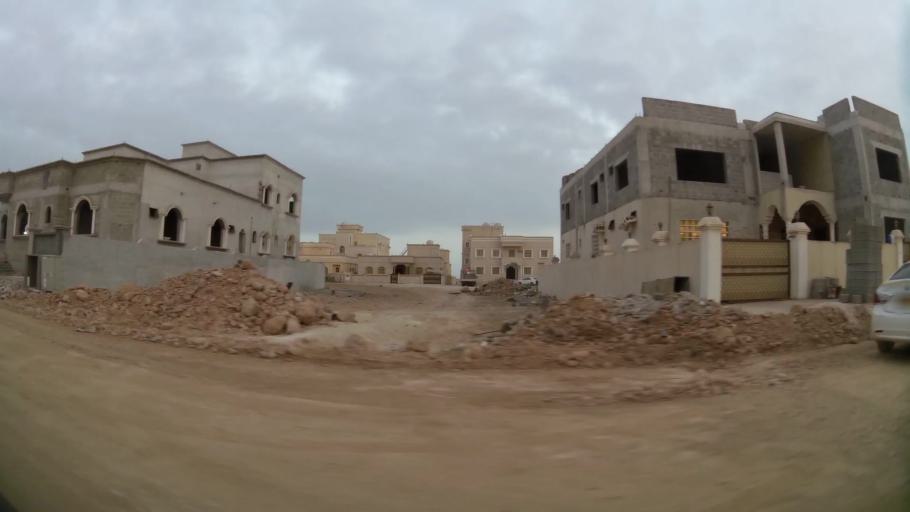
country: OM
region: Zufar
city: Salalah
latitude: 17.0382
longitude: 54.0332
